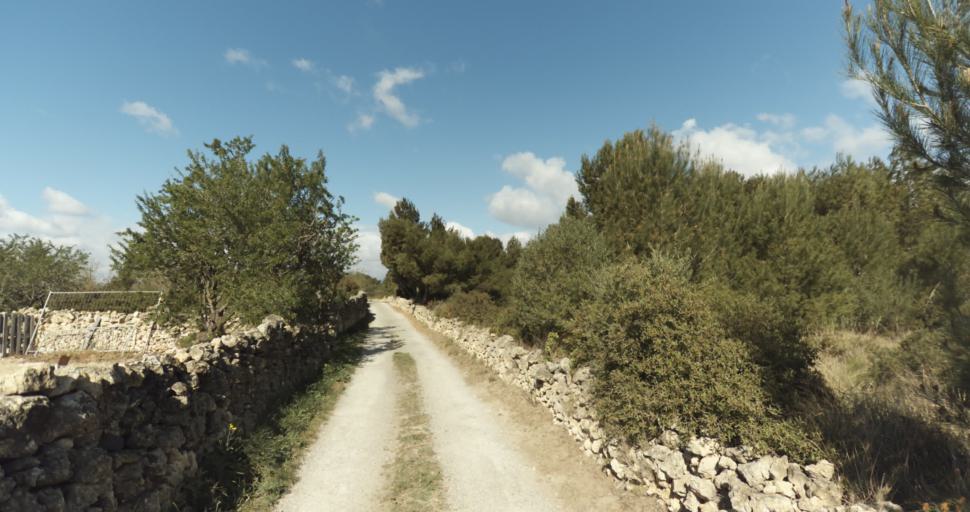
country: FR
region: Languedoc-Roussillon
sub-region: Departement de l'Aude
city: Leucate
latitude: 42.9295
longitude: 3.0303
